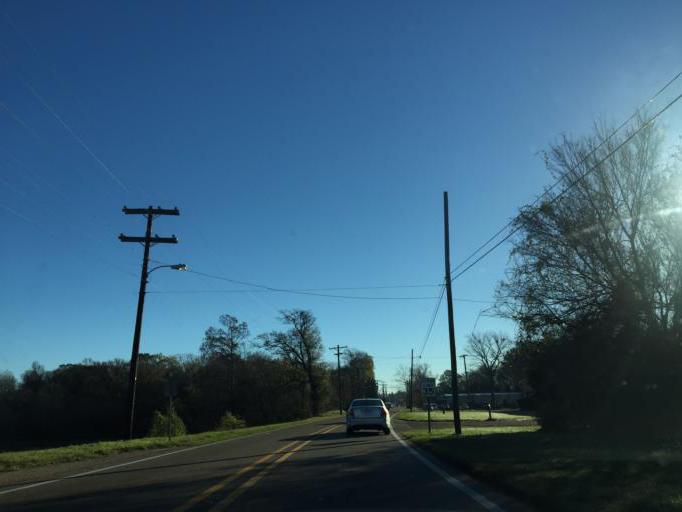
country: US
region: Mississippi
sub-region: Hinds County
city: Jackson
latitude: 32.2830
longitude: -90.1662
